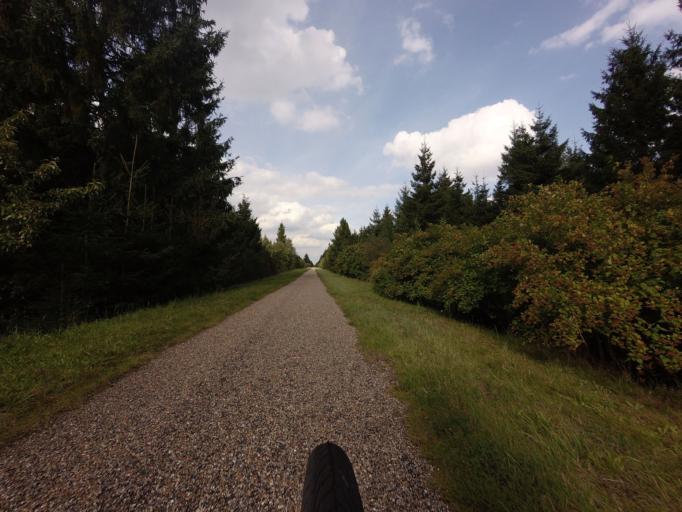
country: DK
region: Central Jutland
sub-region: Viborg Kommune
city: Karup
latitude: 56.2519
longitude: 9.1034
